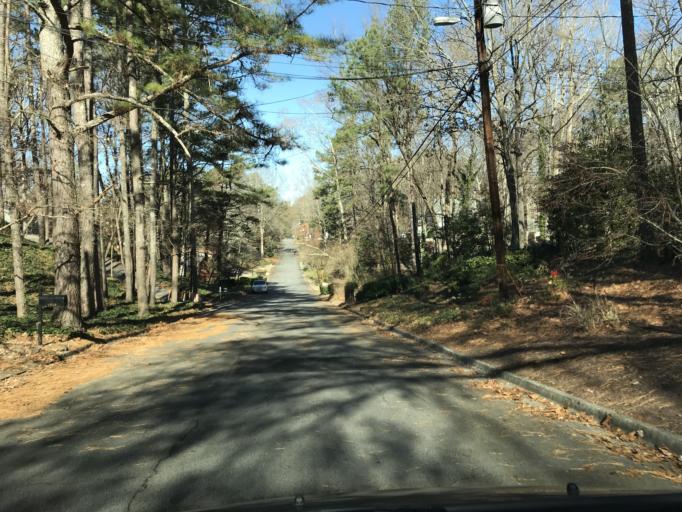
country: US
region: Georgia
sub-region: DeKalb County
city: North Atlanta
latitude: 33.8856
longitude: -84.3489
